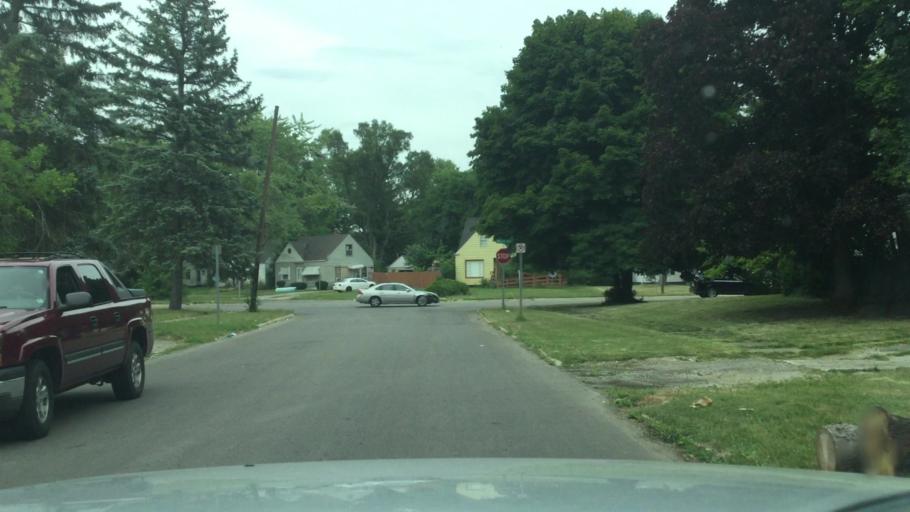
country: US
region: Michigan
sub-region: Genesee County
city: Flint
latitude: 43.0366
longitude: -83.7307
